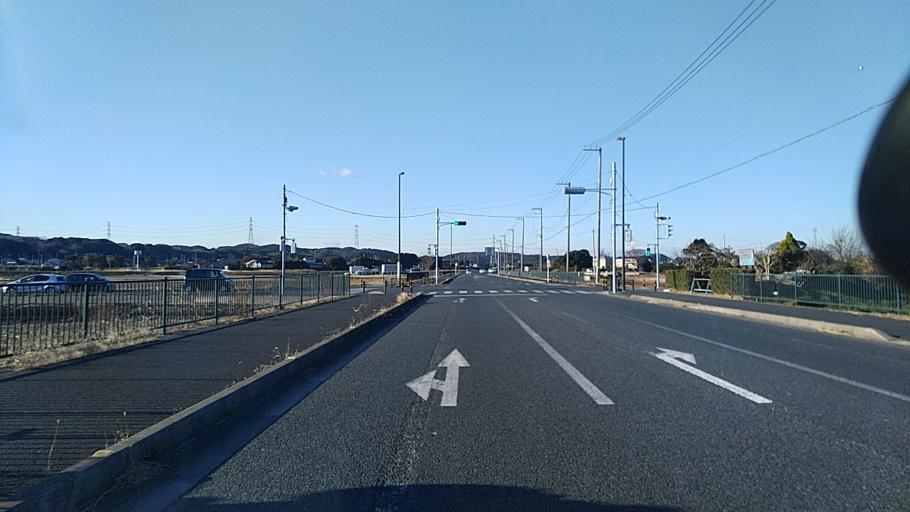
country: JP
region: Chiba
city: Kimitsu
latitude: 35.3250
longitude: 139.8898
